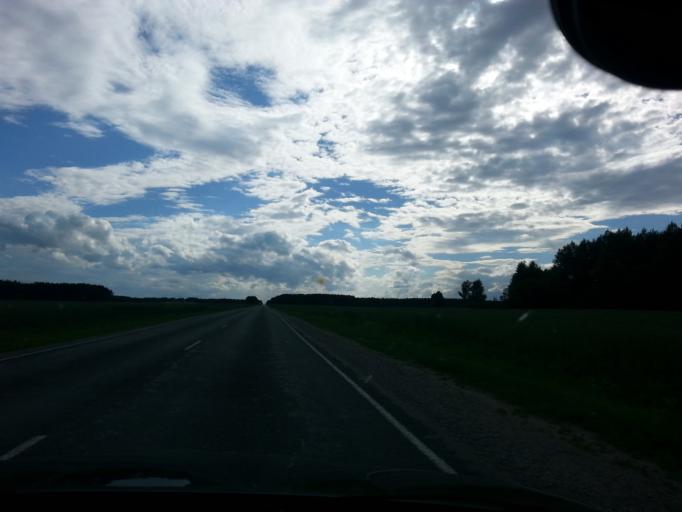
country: BY
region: Grodnenskaya
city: Astravyets
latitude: 54.7990
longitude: 26.1171
